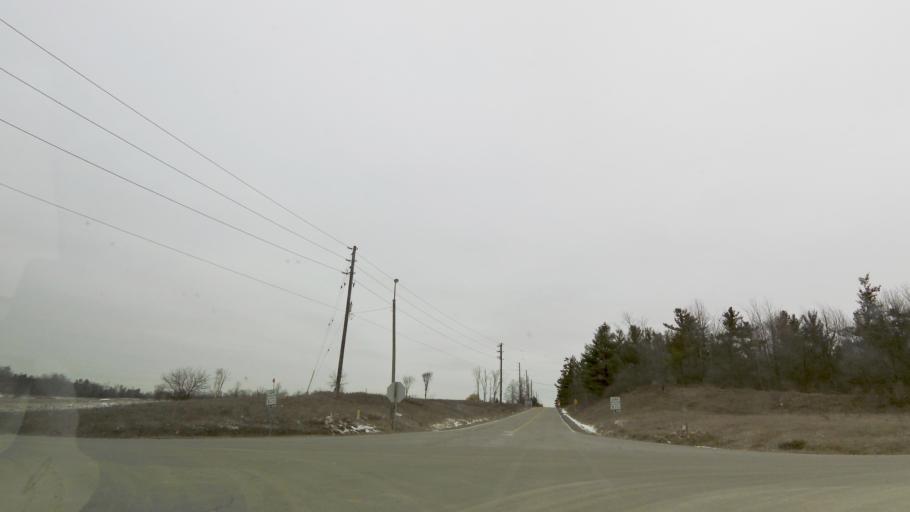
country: CA
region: Ontario
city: Vaughan
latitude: 43.8708
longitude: -79.6187
